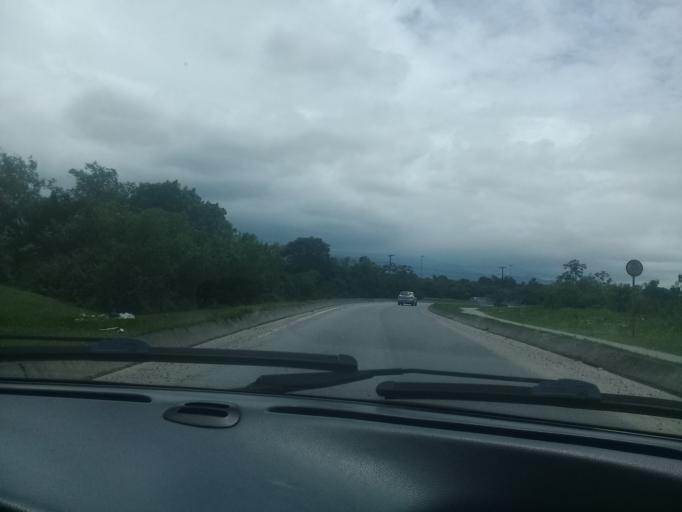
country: BR
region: Sao Paulo
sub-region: Guaruja
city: Guaruja
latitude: -23.9697
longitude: -46.2680
